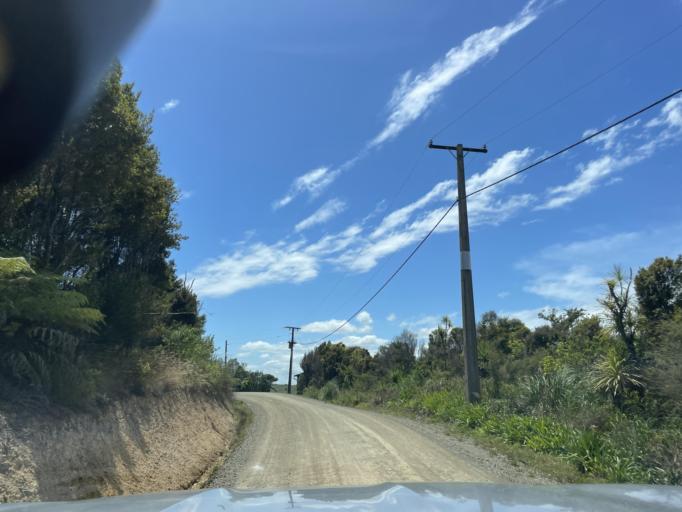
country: NZ
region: Auckland
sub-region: Auckland
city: Wellsford
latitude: -36.2186
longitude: 174.3584
